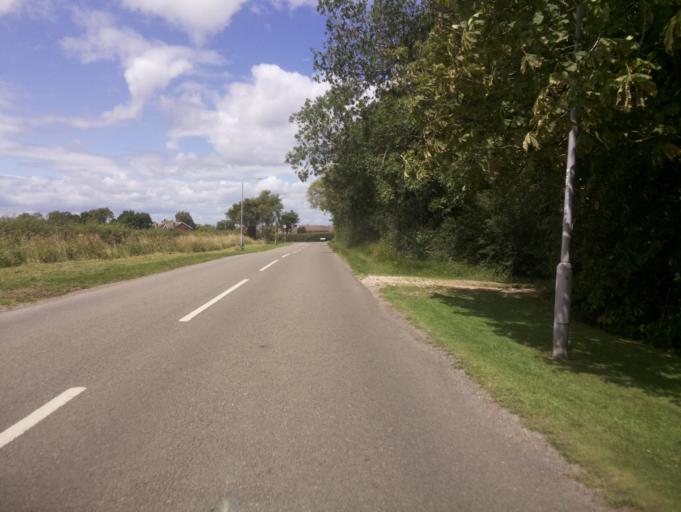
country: GB
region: England
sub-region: Nottinghamshire
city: Cotgrave
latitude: 52.8685
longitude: -1.0733
